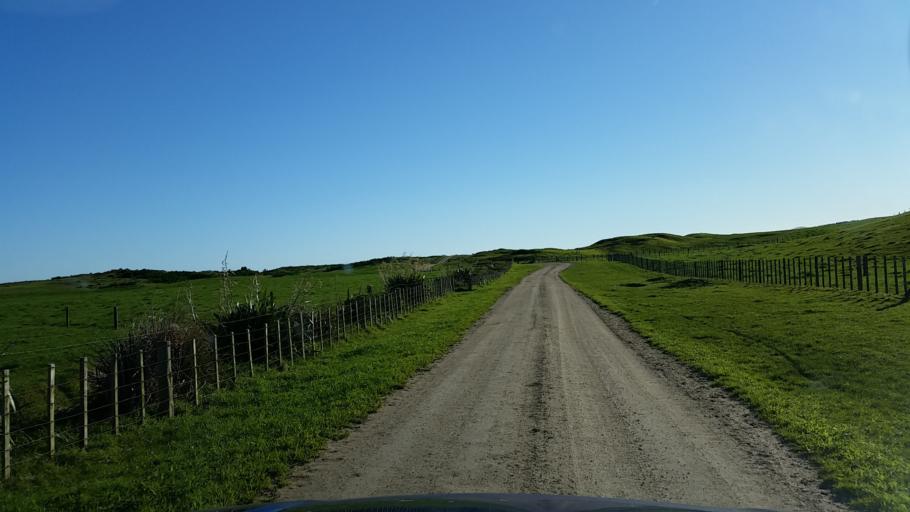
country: NZ
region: Taranaki
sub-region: South Taranaki District
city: Patea
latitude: -39.8375
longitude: 174.6977
